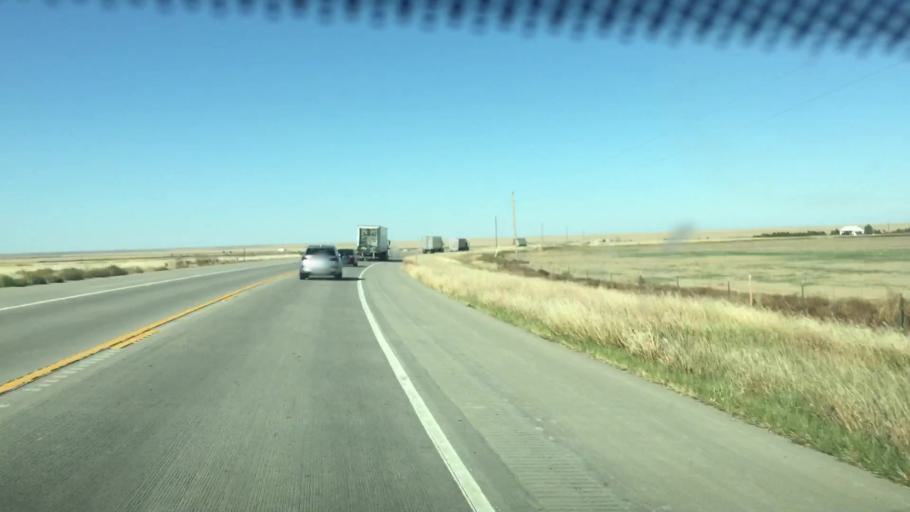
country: US
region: Colorado
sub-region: Kiowa County
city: Eads
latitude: 38.3398
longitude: -102.7198
